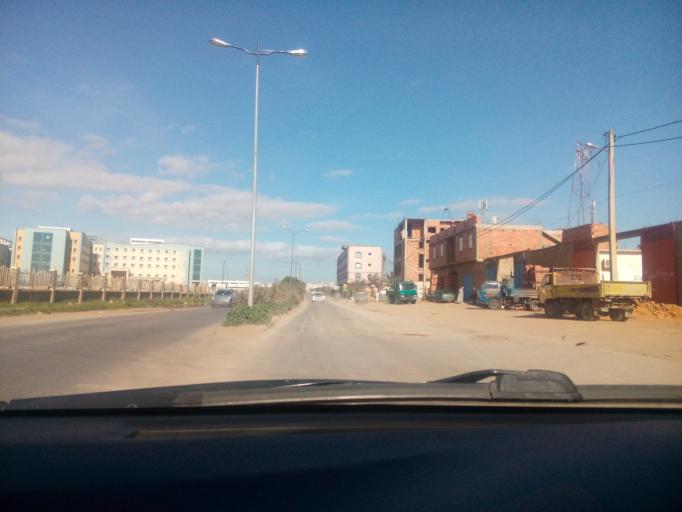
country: DZ
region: Oran
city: Sidi ech Chahmi
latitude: 35.6543
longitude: -0.5678
